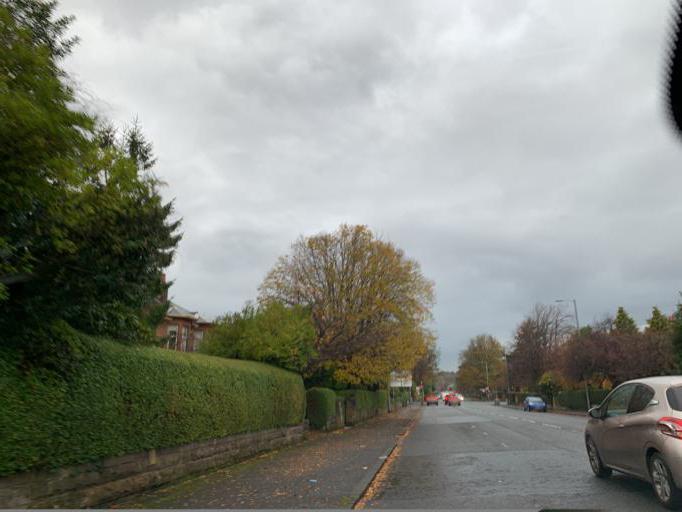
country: GB
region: Scotland
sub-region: East Renfrewshire
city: Giffnock
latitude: 55.8157
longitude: -4.2869
